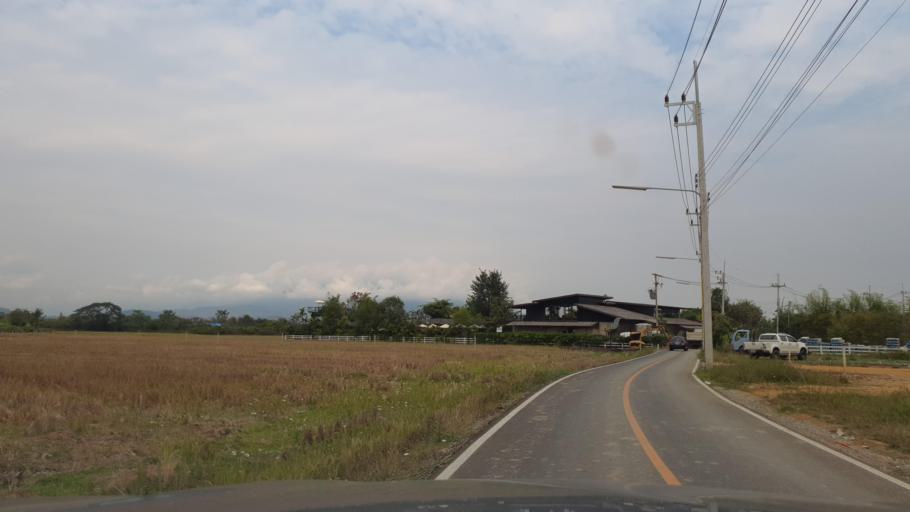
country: TH
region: Chiang Mai
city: Hang Dong
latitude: 18.6795
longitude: 98.9600
